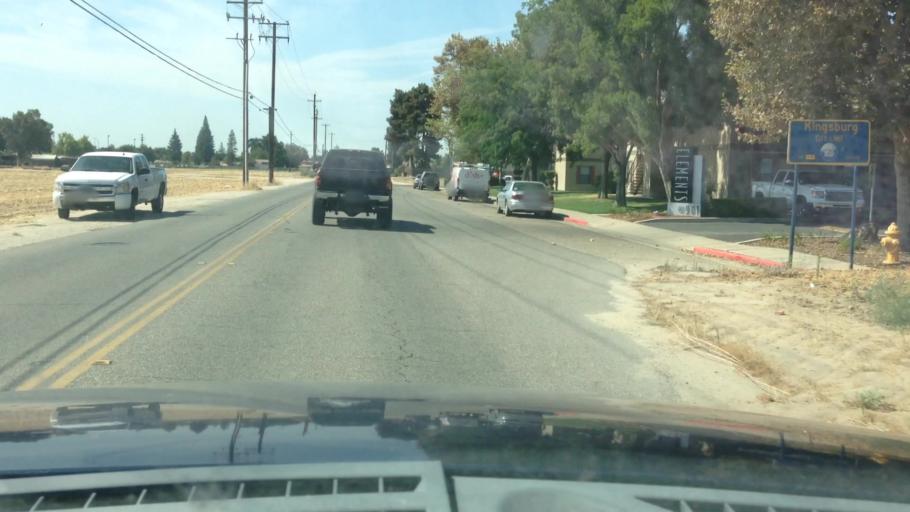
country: US
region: California
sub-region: Fresno County
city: Kingsburg
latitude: 36.5279
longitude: -119.5569
